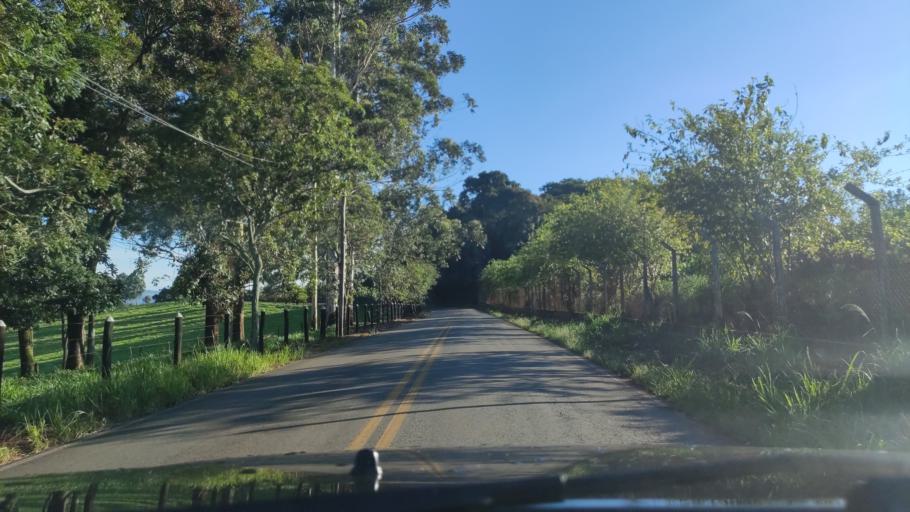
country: BR
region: Sao Paulo
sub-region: Serra Negra
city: Serra Negra
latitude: -22.5882
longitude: -46.6242
